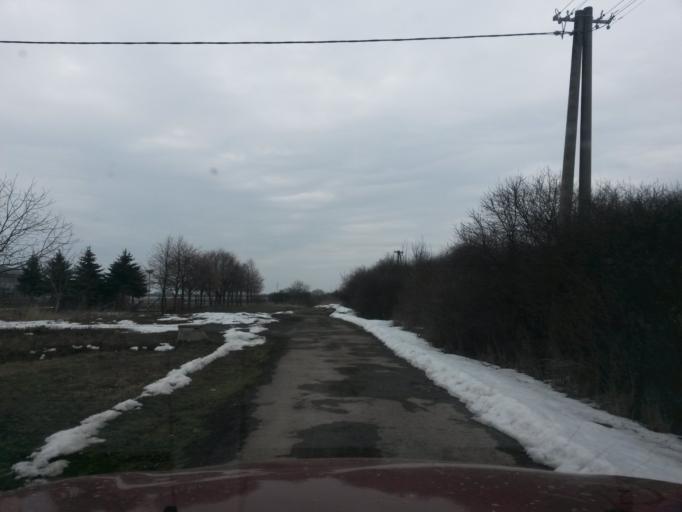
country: SK
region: Kosicky
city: Vinne
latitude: 48.7451
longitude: 22.0226
